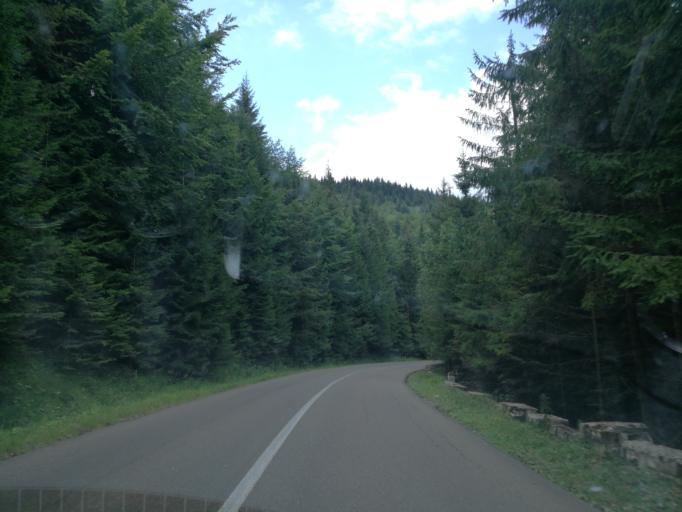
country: RO
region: Suceava
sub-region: Comuna Sucevita
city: Sucevita
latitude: 47.7440
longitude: 25.6415
